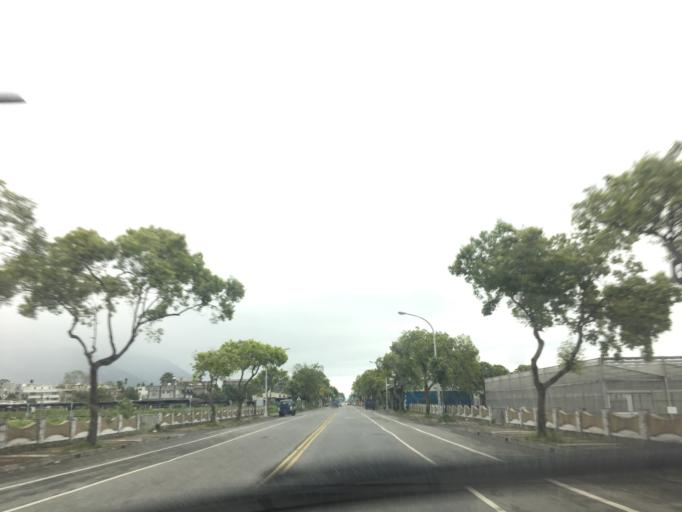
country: TW
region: Taiwan
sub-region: Hualien
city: Hualian
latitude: 23.9754
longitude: 121.5645
